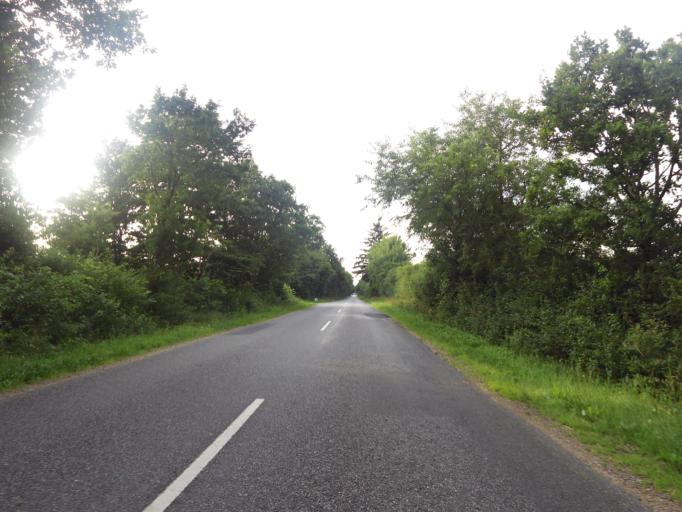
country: DK
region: South Denmark
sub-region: Tonder Kommune
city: Sherrebek
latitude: 55.1919
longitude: 8.8973
